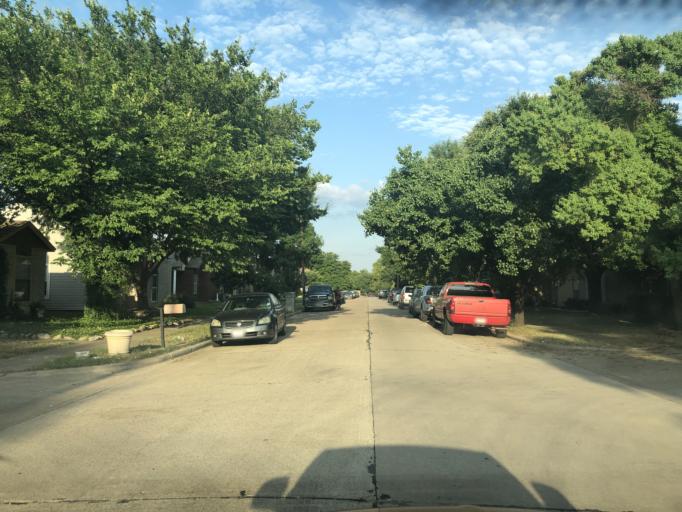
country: US
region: Texas
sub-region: Dallas County
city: Irving
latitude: 32.7905
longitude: -96.9457
